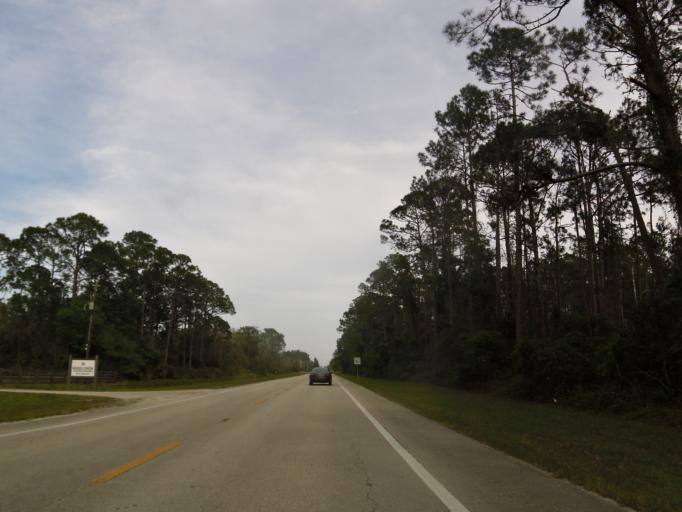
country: US
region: Florida
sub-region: Saint Johns County
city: Butler Beach
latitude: 29.7567
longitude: -81.2953
